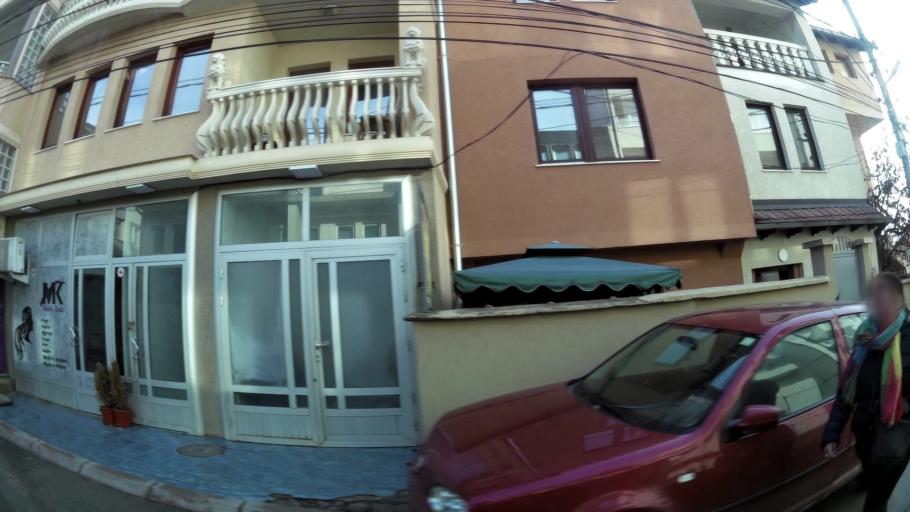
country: XK
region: Pristina
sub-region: Komuna e Prishtines
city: Pristina
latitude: 42.6683
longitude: 21.1842
